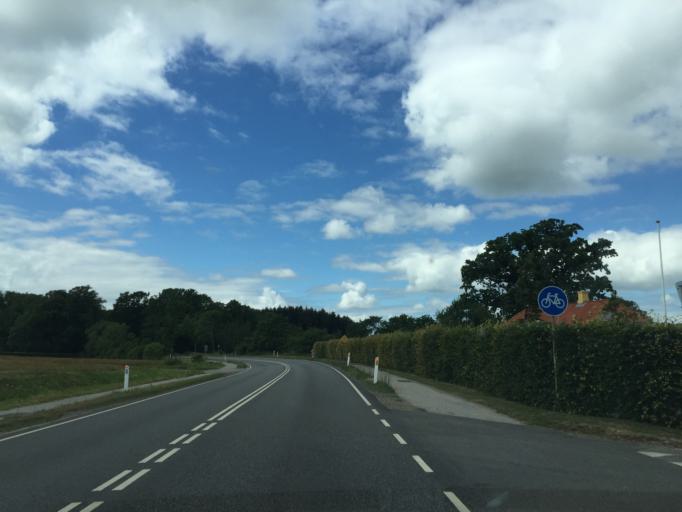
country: DK
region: South Denmark
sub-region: Svendborg Kommune
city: Svendborg
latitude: 55.0740
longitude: 10.5564
